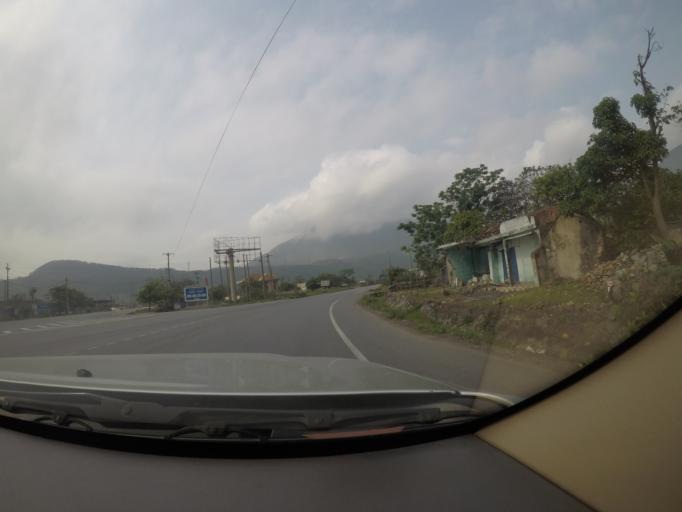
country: VN
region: Ha Tinh
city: Ky Anh
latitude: 17.9677
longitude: 106.4709
